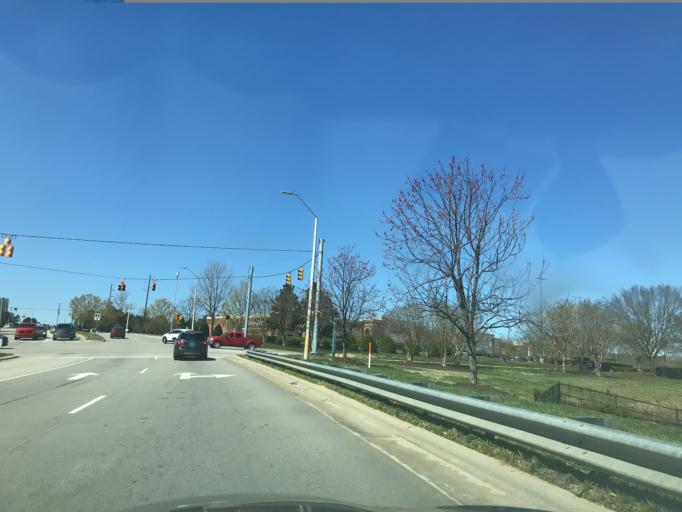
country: US
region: North Carolina
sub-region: Wake County
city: Garner
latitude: 35.6897
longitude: -78.5794
